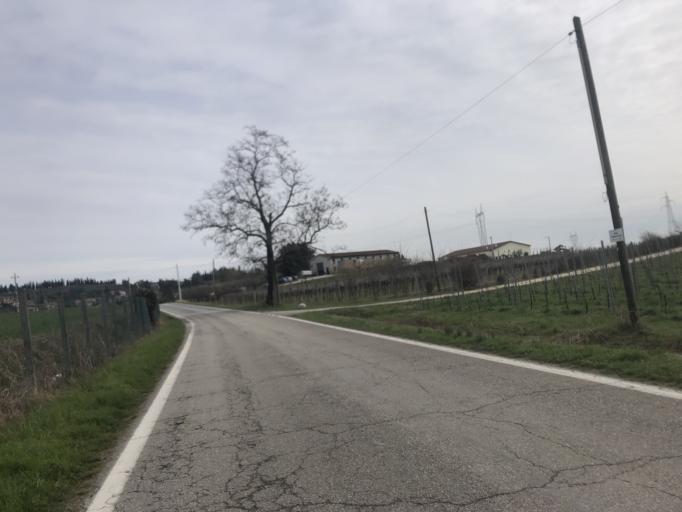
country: IT
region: Veneto
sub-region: Provincia di Verona
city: Sona
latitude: 45.4343
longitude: 10.8163
